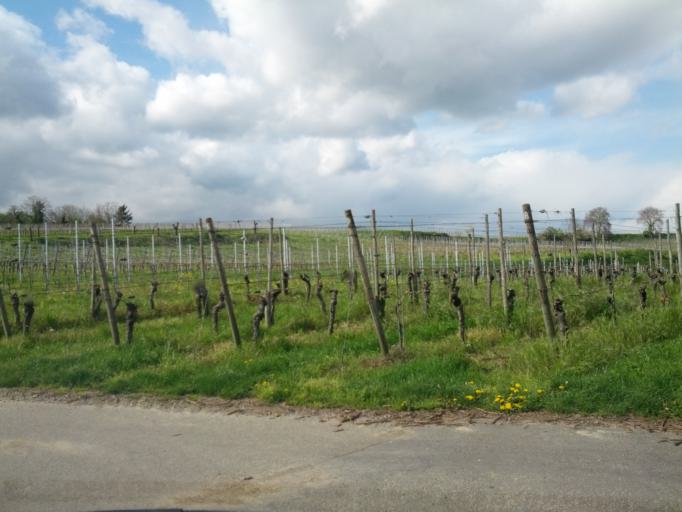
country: DE
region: Baden-Wuerttemberg
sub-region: Freiburg Region
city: Merdingen
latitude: 47.9870
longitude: 7.6837
